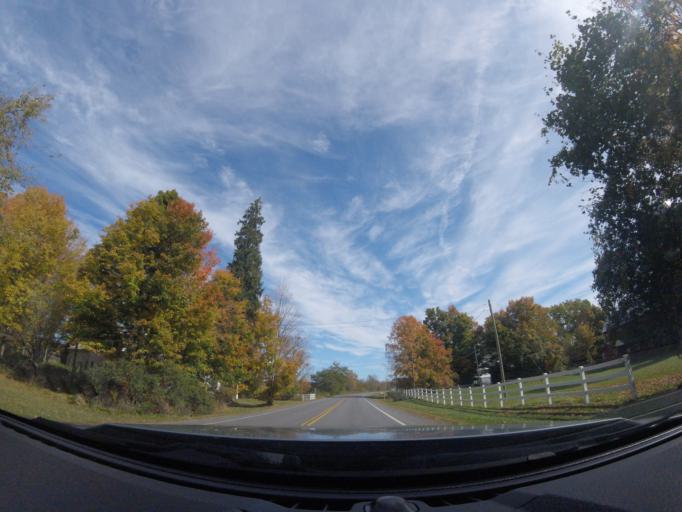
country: US
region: New York
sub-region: Tompkins County
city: Dryden
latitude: 42.5292
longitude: -76.3169
